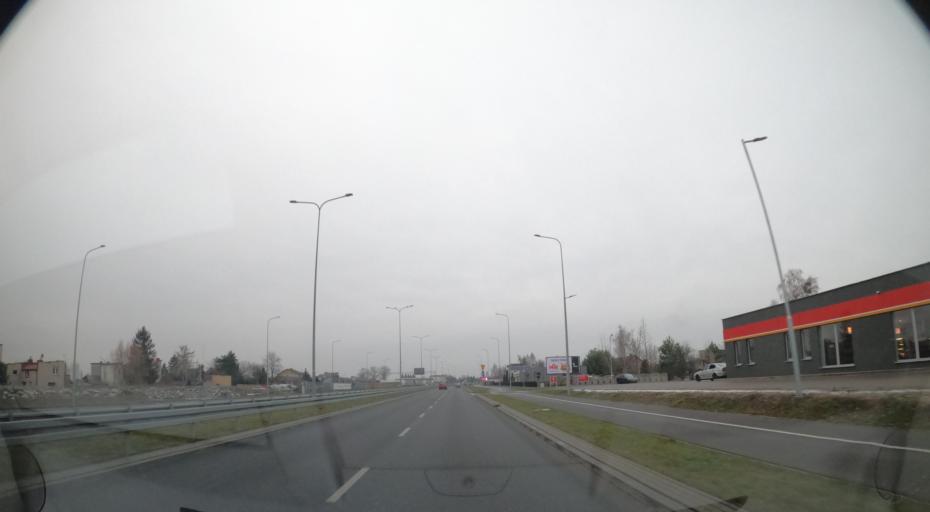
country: PL
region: Masovian Voivodeship
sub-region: Radom
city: Radom
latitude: 51.3922
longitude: 21.1947
